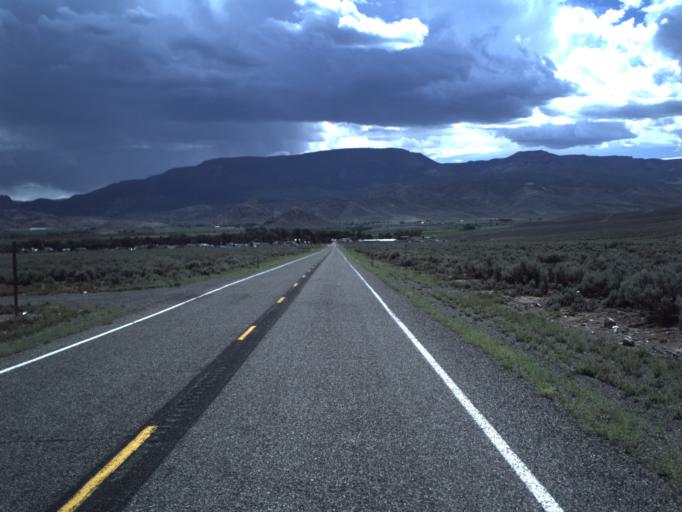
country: US
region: Utah
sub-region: Piute County
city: Junction
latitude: 38.2511
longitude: -112.2397
